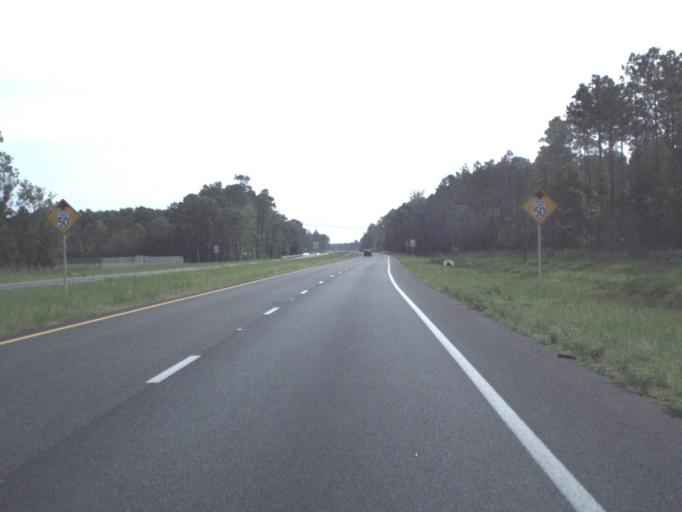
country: US
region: Florida
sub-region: Duval County
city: Baldwin
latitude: 30.3723
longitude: -81.9434
